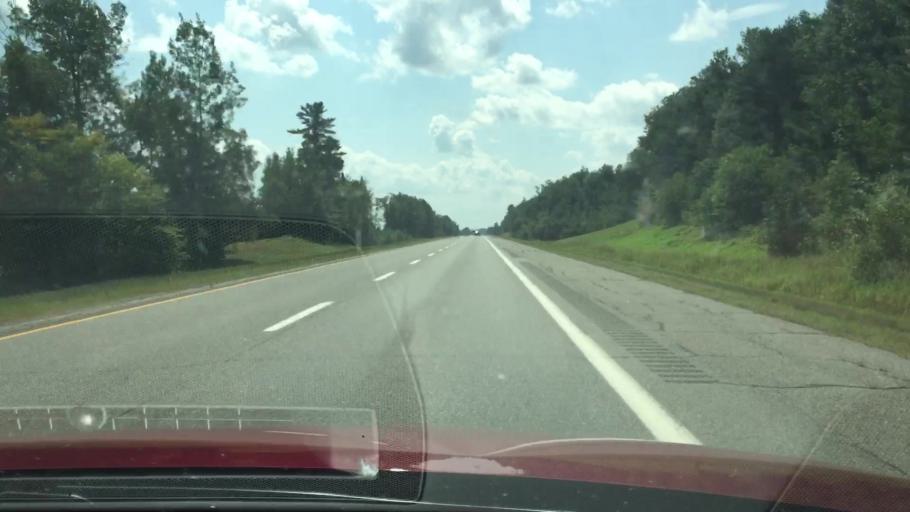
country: US
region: Maine
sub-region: Penobscot County
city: Medway
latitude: 45.5010
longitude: -68.5587
